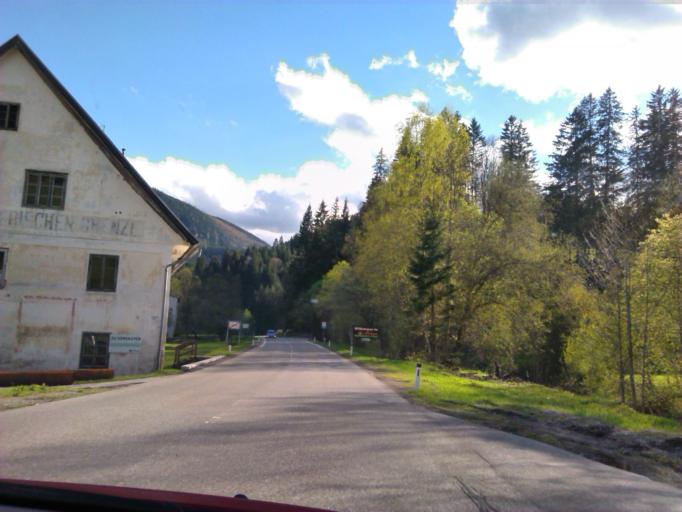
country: AT
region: Styria
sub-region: Politischer Bezirk Bruck-Muerzzuschlag
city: Muerzsteg
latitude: 47.7725
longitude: 15.4497
